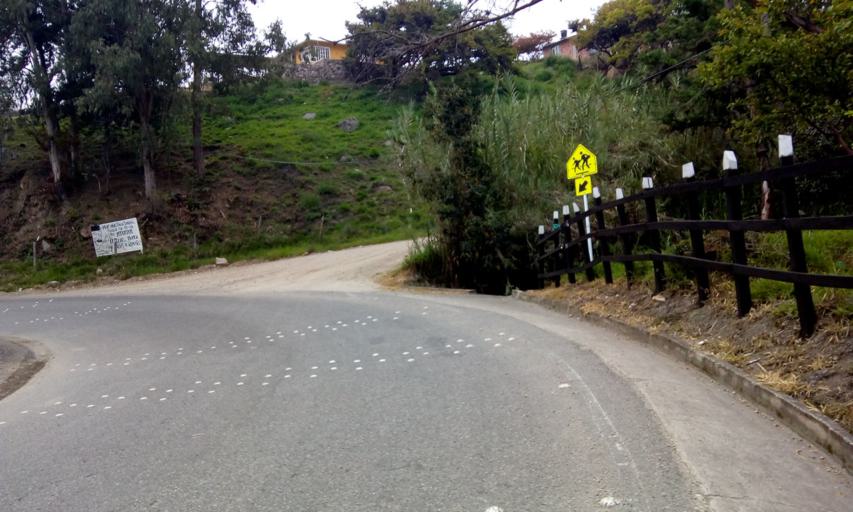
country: CO
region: Boyaca
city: Tipacoque
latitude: 6.4145
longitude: -72.6886
